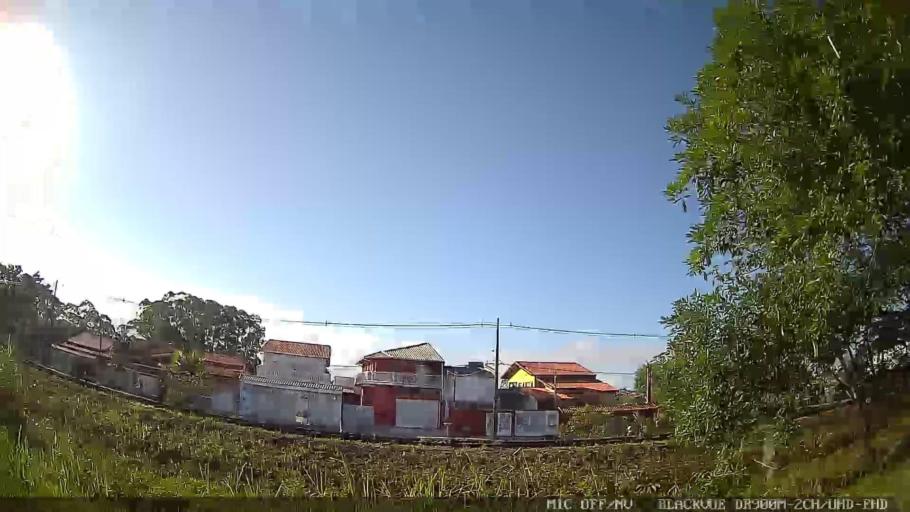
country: BR
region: Sao Paulo
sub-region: Peruibe
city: Peruibe
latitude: -24.2927
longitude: -46.9757
